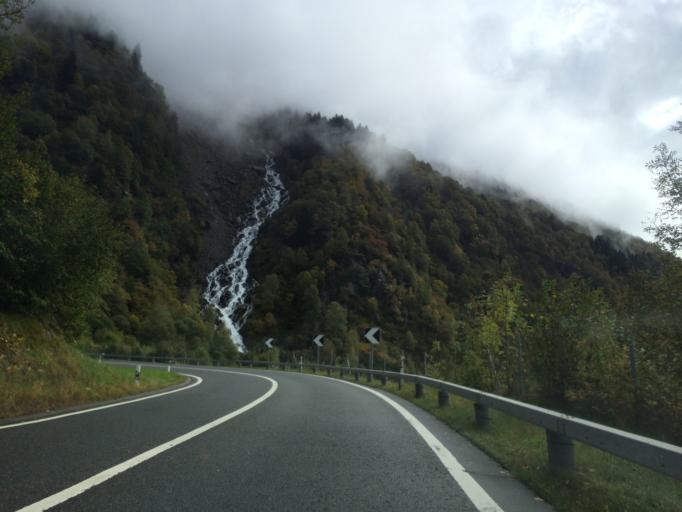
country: CH
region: Grisons
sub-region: Moesa District
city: Mesocco
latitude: 46.4081
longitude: 9.2377
